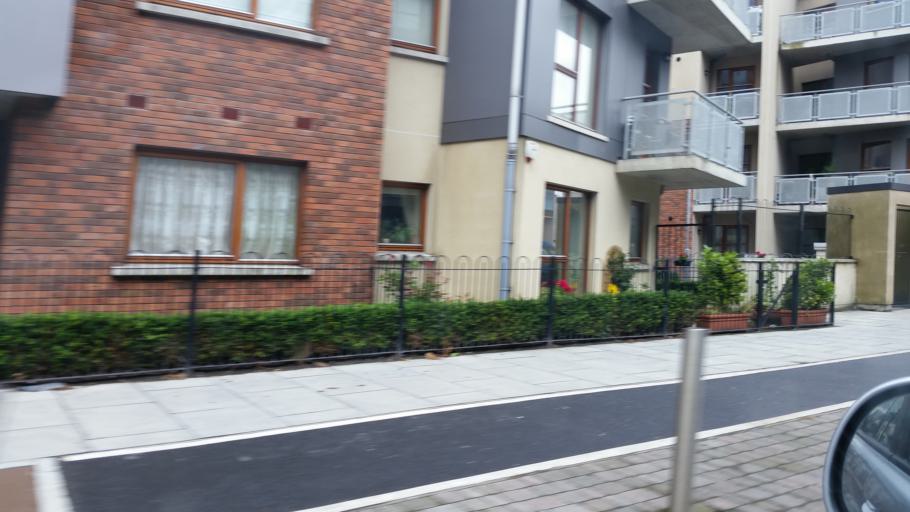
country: IE
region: Leinster
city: Tallaght
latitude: 53.2862
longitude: -6.3766
